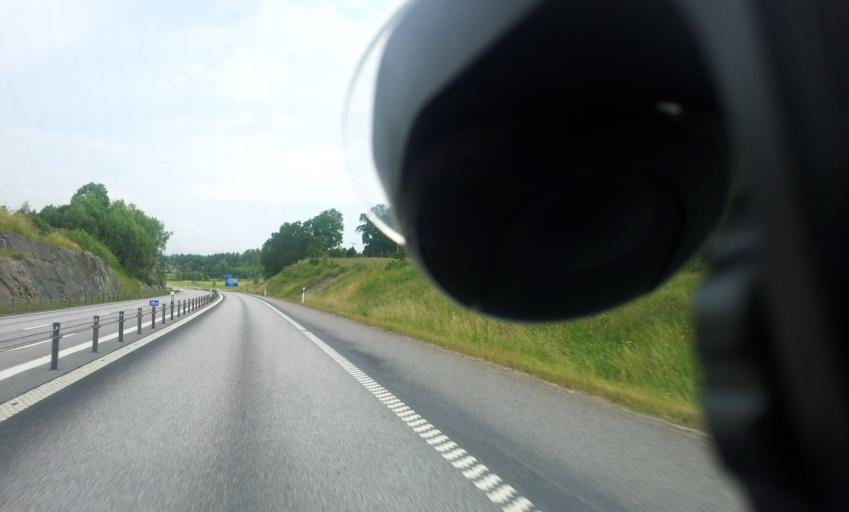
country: SE
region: OEstergoetland
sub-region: Valdemarsviks Kommun
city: Gusum
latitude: 58.2746
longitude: 16.5160
